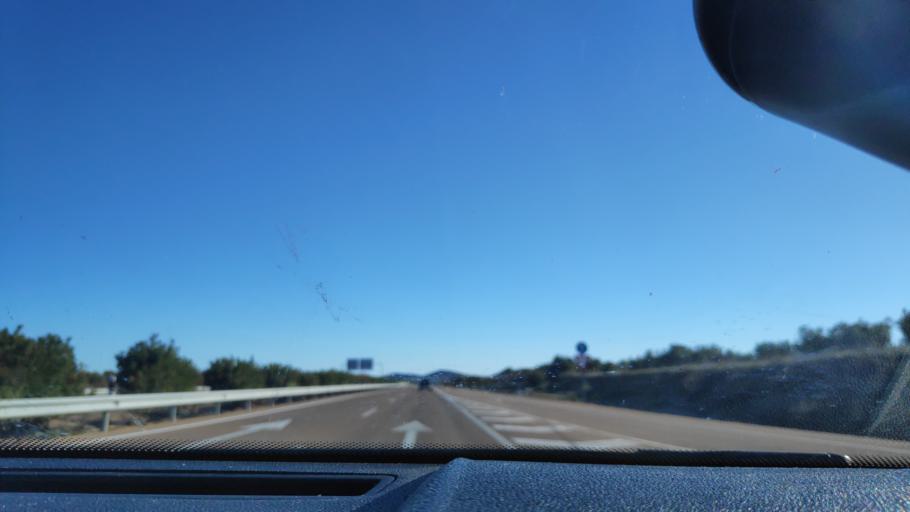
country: ES
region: Extremadura
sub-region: Provincia de Badajoz
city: Los Santos de Maimona
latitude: 38.4590
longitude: -6.3531
